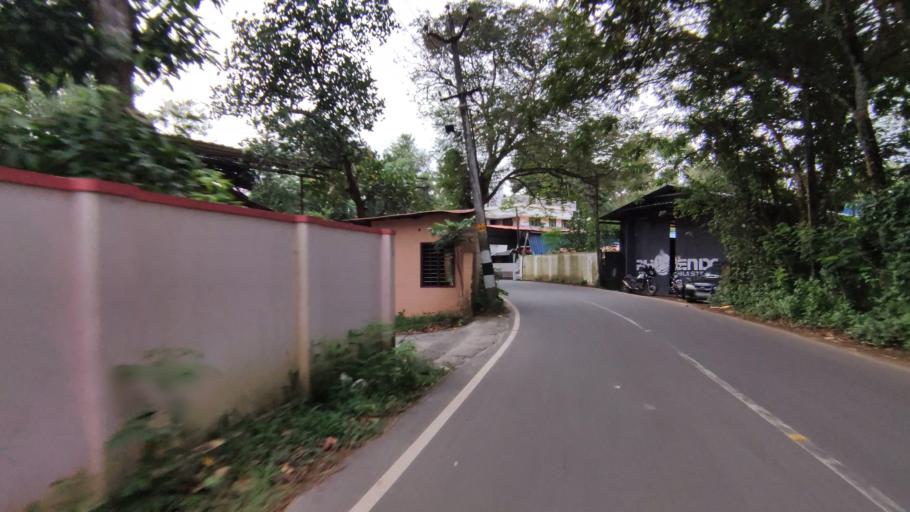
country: IN
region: Kerala
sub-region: Alappuzha
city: Shertallai
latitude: 9.6558
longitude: 76.3691
